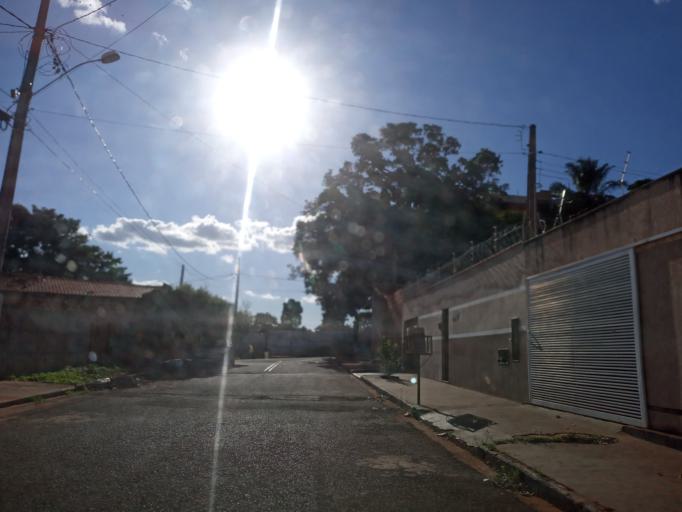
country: BR
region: Minas Gerais
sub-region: Ituiutaba
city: Ituiutaba
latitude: -18.9733
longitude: -49.4488
